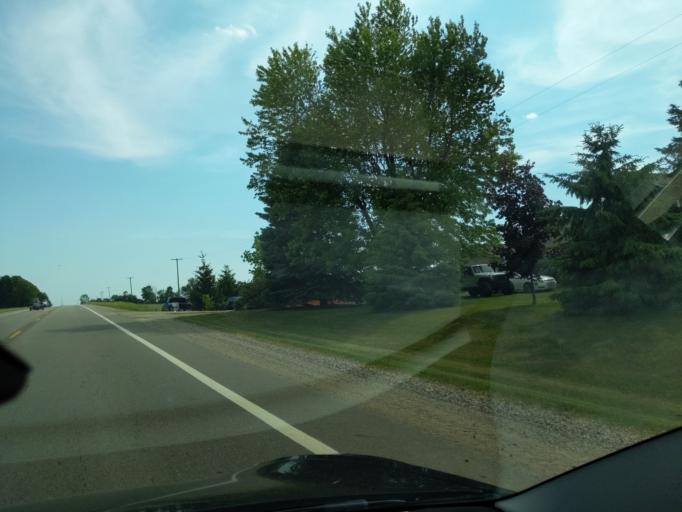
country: US
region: Michigan
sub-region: Barry County
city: Nashville
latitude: 42.6360
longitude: -85.0949
